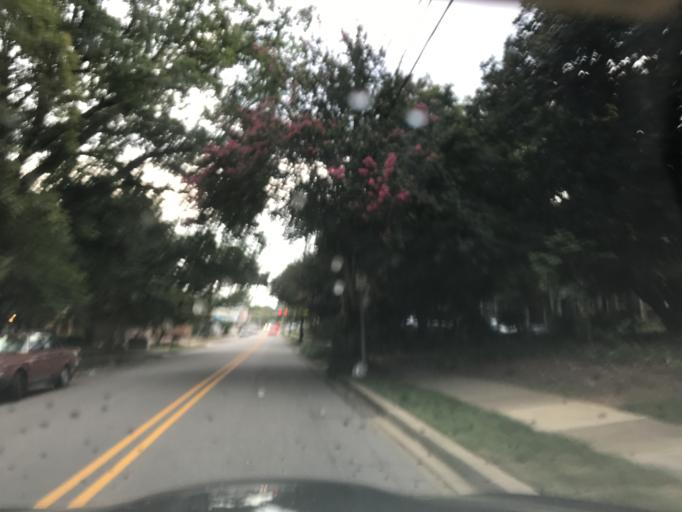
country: US
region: North Carolina
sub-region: Wake County
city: West Raleigh
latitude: 35.8056
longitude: -78.6483
